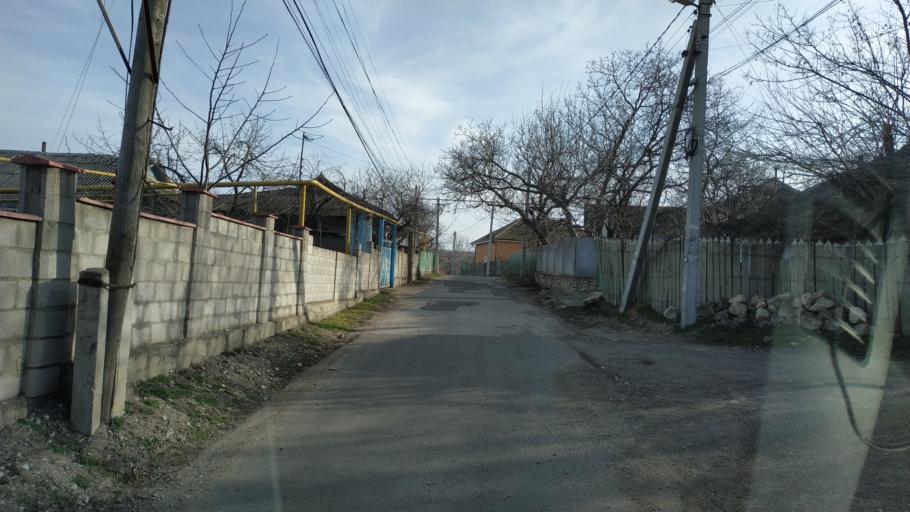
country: MD
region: Chisinau
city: Vatra
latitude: 47.0708
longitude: 28.6734
